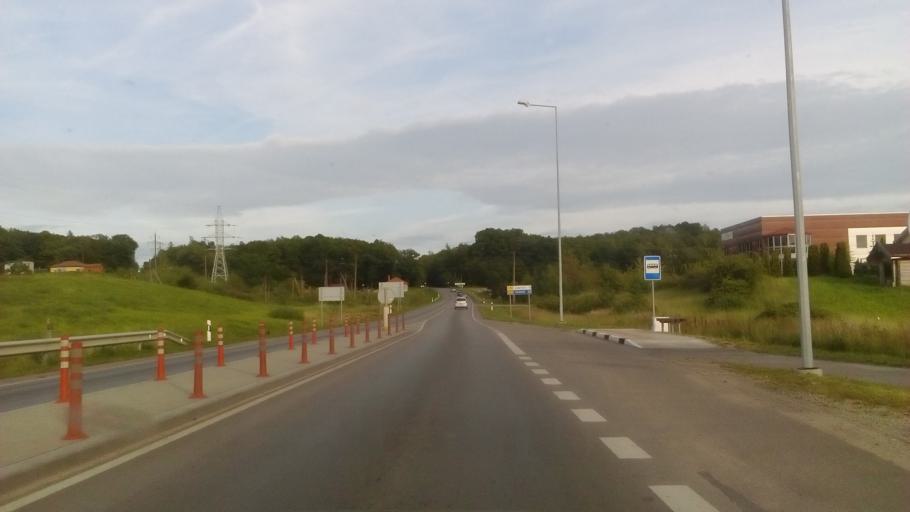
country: LT
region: Alytaus apskritis
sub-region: Alytus
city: Alytus
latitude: 54.3880
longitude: 23.9976
